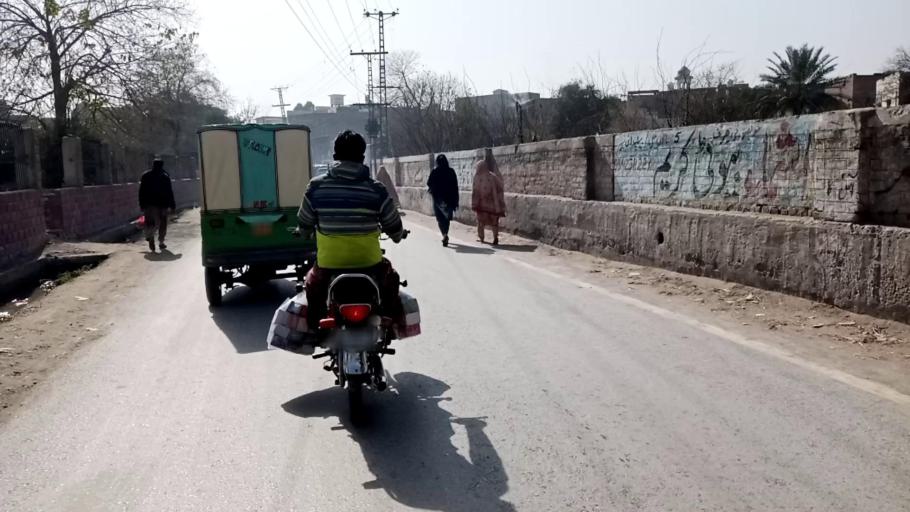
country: PK
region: Khyber Pakhtunkhwa
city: Peshawar
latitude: 34.0036
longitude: 71.5851
